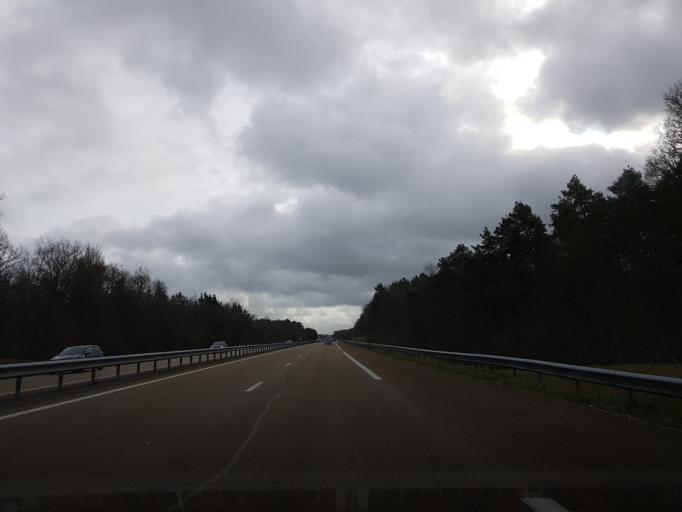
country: FR
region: Champagne-Ardenne
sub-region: Departement de la Haute-Marne
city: Chamarandes-Choignes
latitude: 47.9919
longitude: 5.1249
